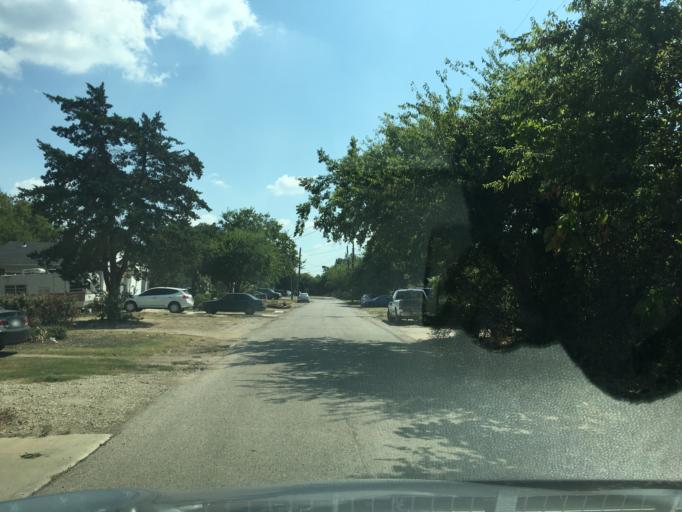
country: US
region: Texas
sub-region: Dallas County
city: Dallas
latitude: 32.7394
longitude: -96.7951
